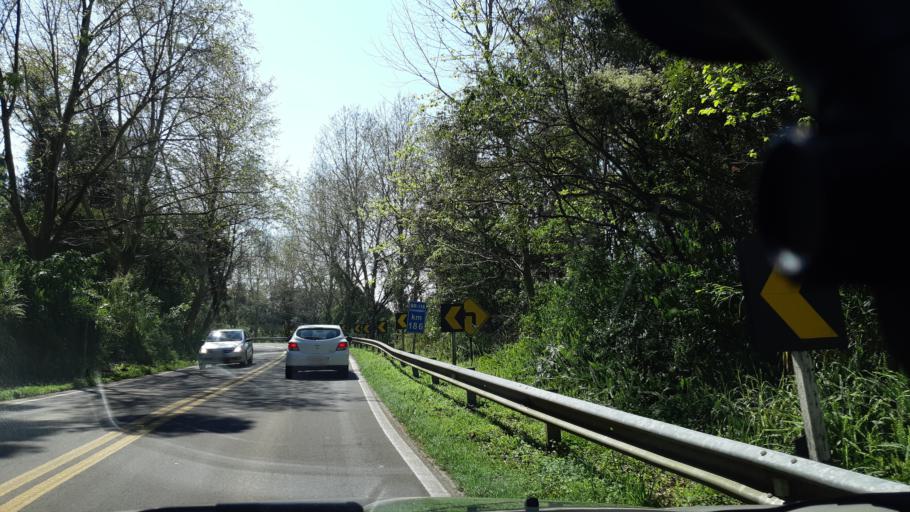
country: BR
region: Rio Grande do Sul
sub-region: Nova Petropolis
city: Nova Petropolis
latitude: -29.3948
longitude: -51.1239
